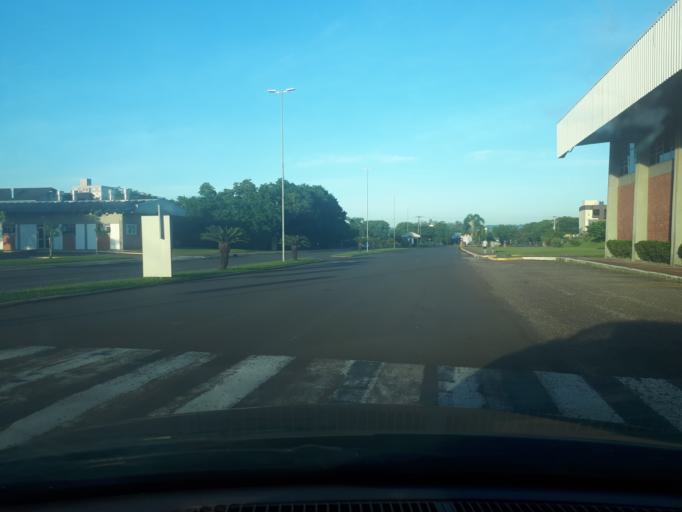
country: BR
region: Rio Grande do Sul
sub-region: Santa Cruz Do Sul
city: Santa Cruz do Sul
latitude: -29.6985
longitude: -52.4400
